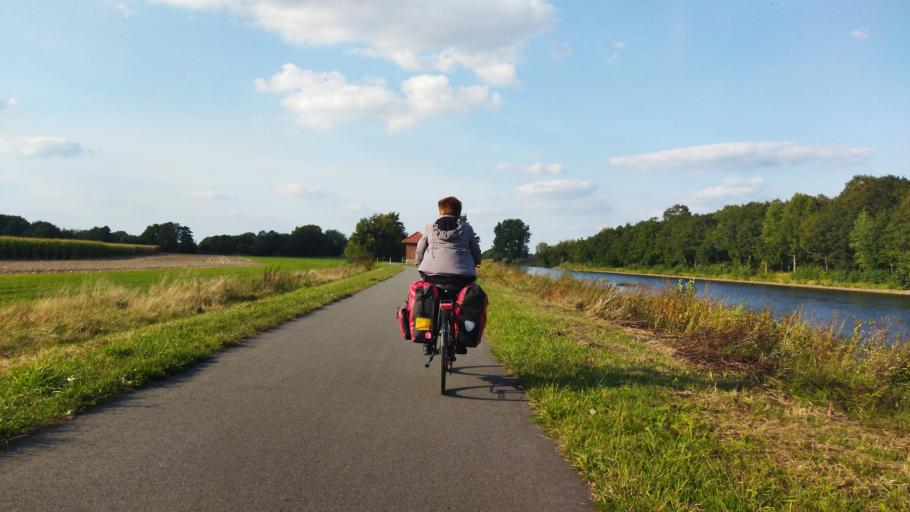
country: DE
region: Lower Saxony
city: Lehe
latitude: 53.0204
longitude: 7.3213
